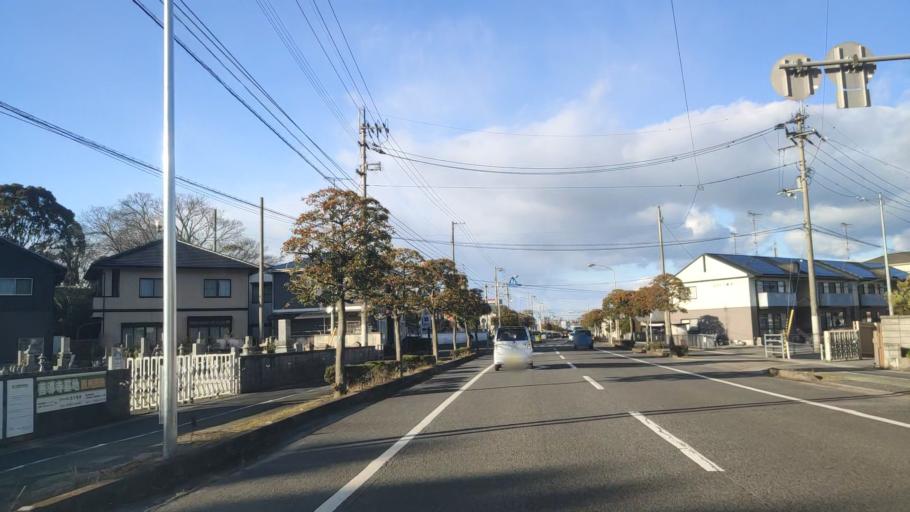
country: JP
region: Ehime
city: Saijo
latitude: 33.9225
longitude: 133.1842
